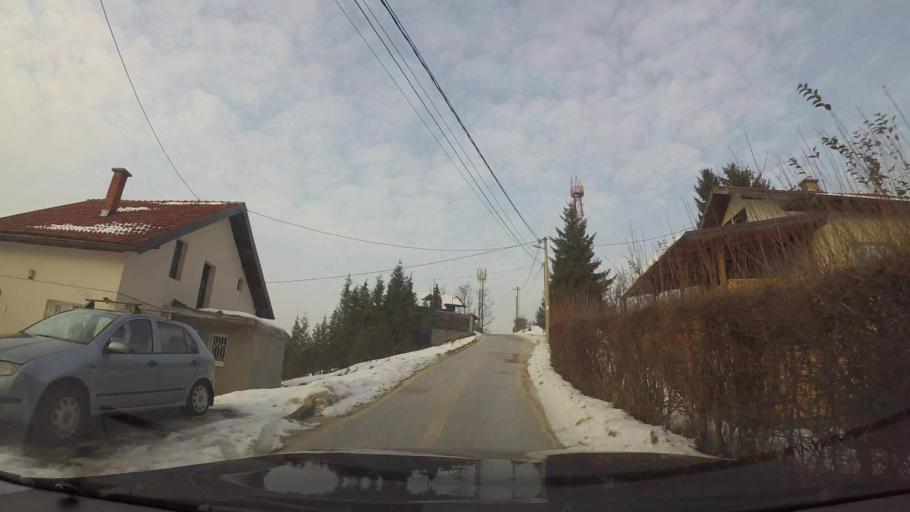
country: BA
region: Federation of Bosnia and Herzegovina
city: Hotonj
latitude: 43.8897
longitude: 18.3812
